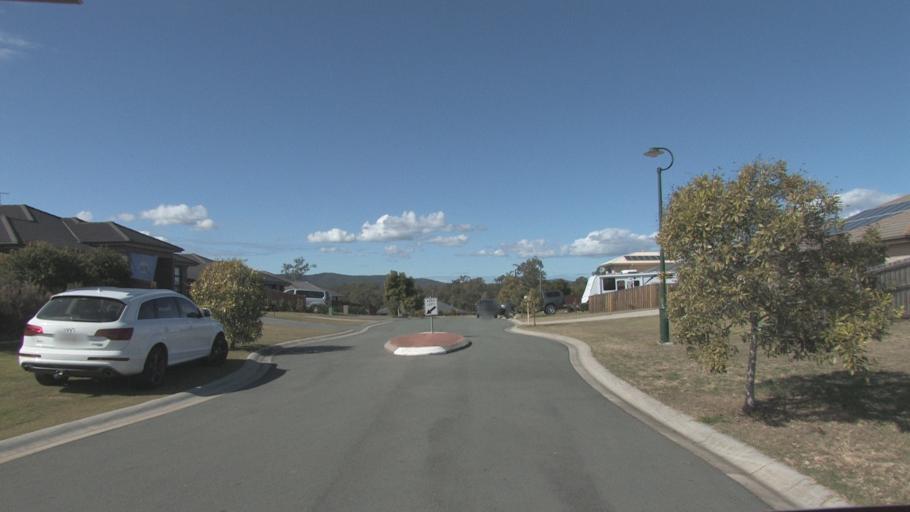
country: AU
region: Queensland
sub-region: Logan
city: Chambers Flat
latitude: -27.7726
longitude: 153.1030
